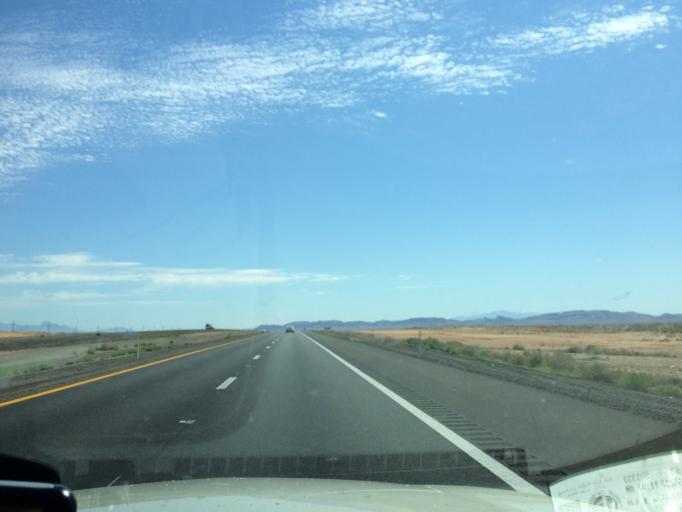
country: US
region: Nevada
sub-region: Clark County
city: Moapa Town
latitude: 36.4854
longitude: -114.7946
